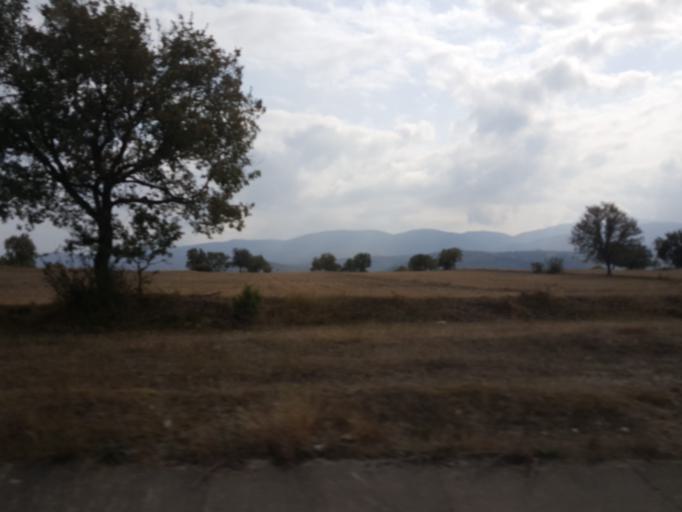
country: TR
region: Sinop
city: Sarayduzu
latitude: 41.3345
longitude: 34.7816
